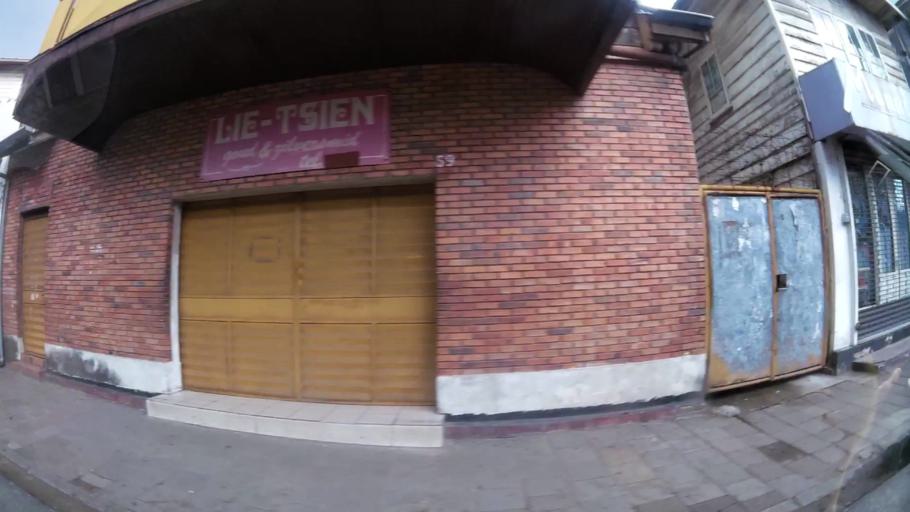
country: SR
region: Paramaribo
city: Paramaribo
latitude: 5.8255
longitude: -55.1625
